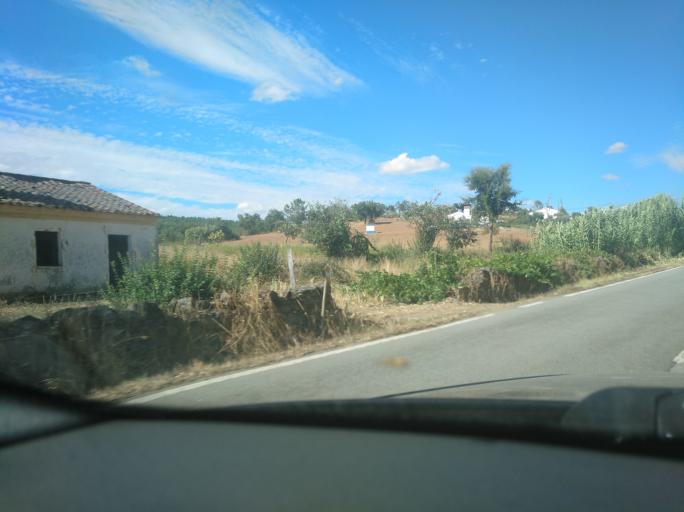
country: ES
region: Extremadura
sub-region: Provincia de Badajoz
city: La Codosera
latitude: 39.1667
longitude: -7.1838
